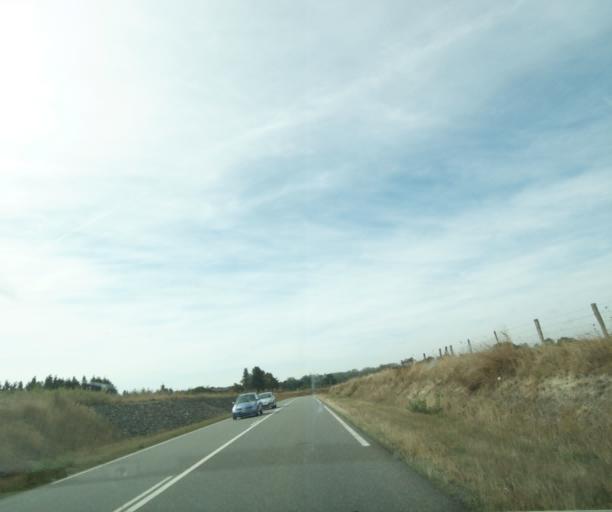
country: FR
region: Auvergne
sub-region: Departement de l'Allier
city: Saint-Gerand-le-Puy
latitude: 46.2142
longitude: 3.5482
